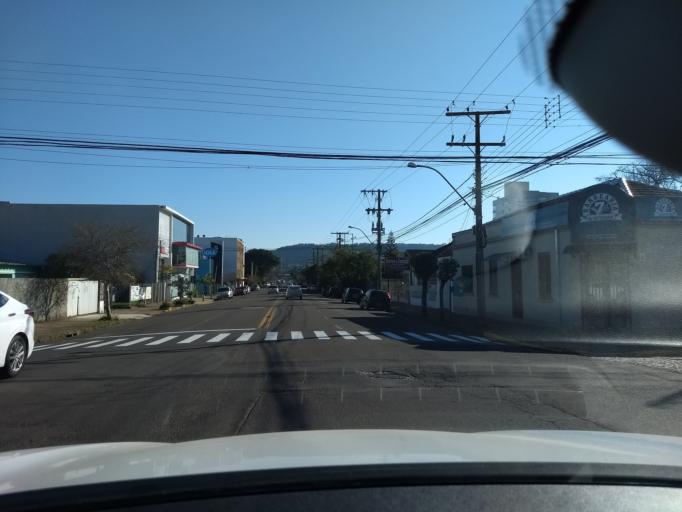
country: BR
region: Rio Grande do Sul
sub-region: Santa Cruz Do Sul
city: Santa Cruz do Sul
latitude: -29.7132
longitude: -52.4357
